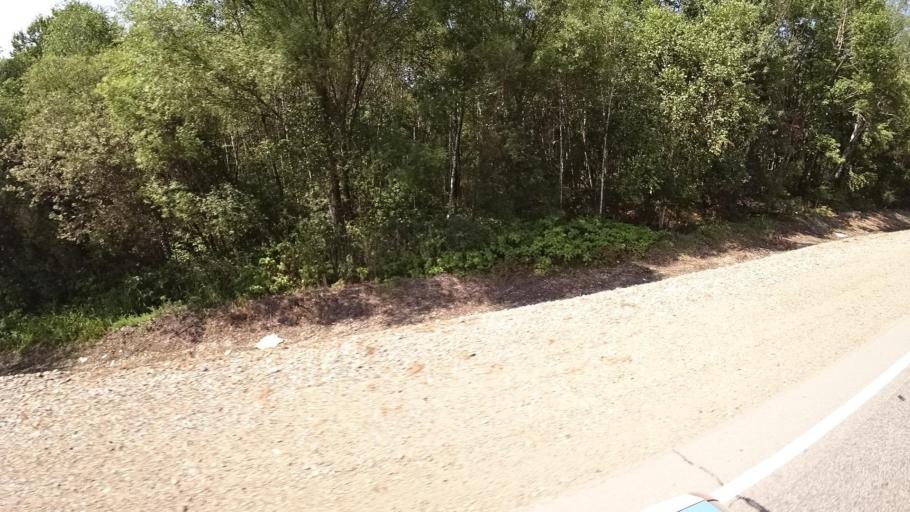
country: RU
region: Khabarovsk Krai
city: Khor
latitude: 47.9832
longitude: 135.0879
